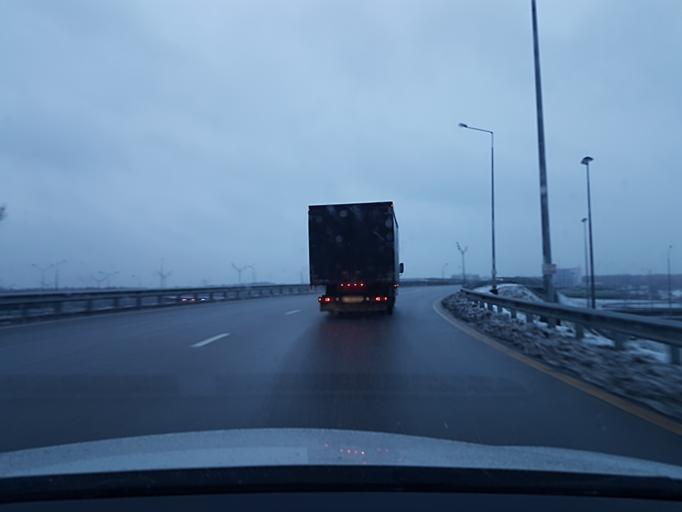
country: RU
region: Moscow
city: Khimki
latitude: 55.9584
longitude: 37.4179
